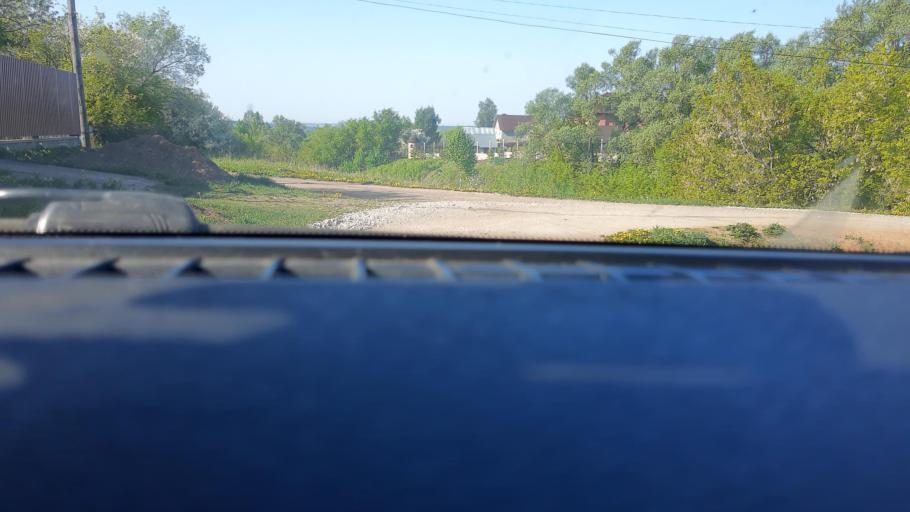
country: RU
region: Bashkortostan
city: Kabakovo
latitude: 54.7121
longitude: 56.2508
